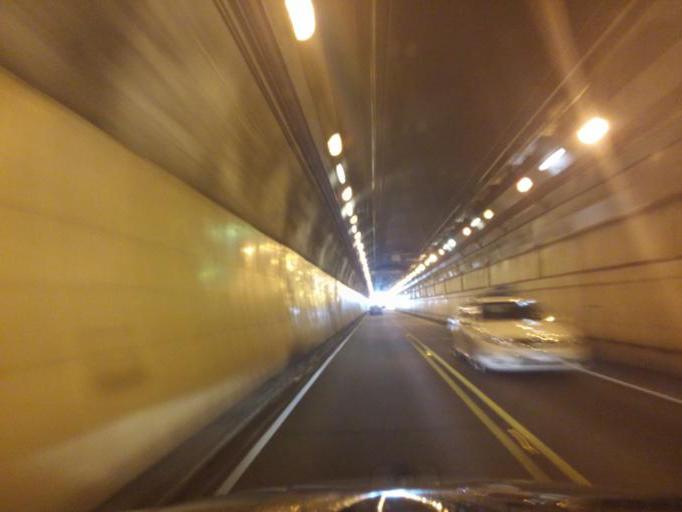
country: NZ
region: Wellington
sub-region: Wellington City
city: Wellington
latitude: -41.3040
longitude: 174.7910
